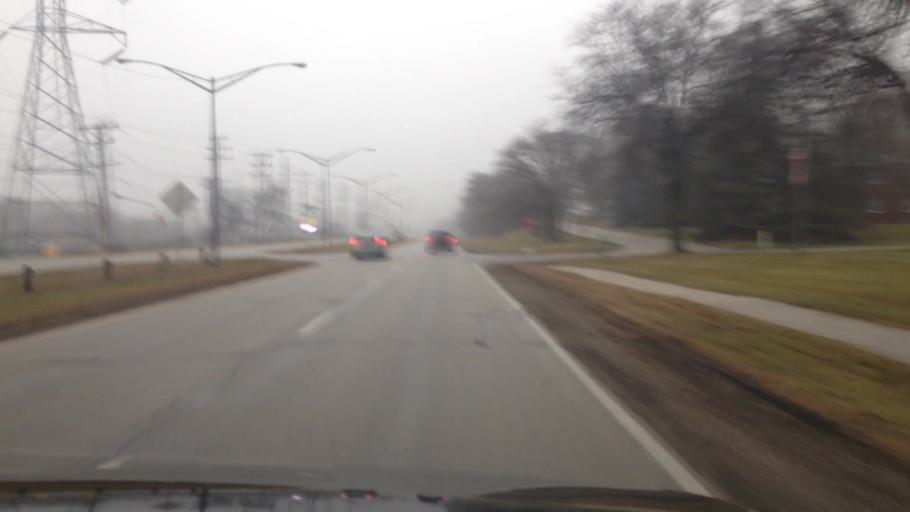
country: US
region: Wisconsin
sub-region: Milwaukee County
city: Hales Corners
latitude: 42.9324
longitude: -88.0516
